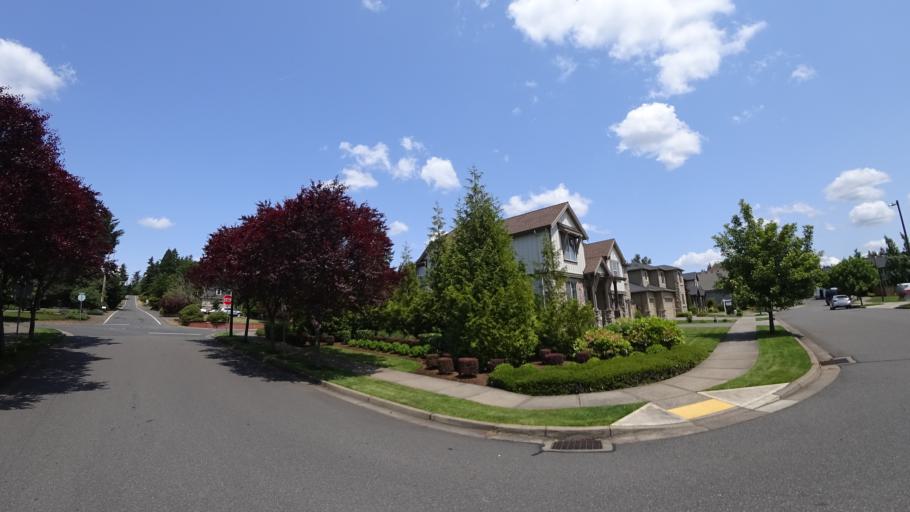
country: US
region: Oregon
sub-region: Clackamas County
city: Happy Valley
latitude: 45.4465
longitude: -122.5496
